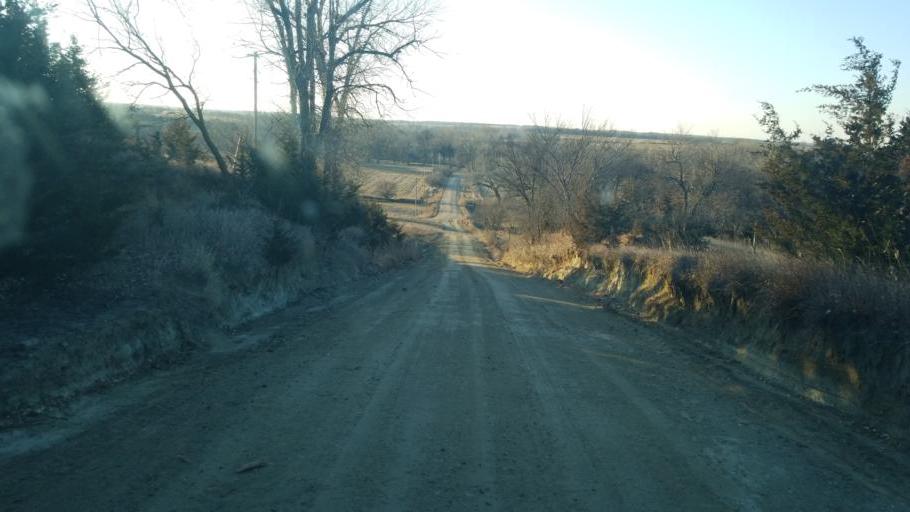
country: US
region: Nebraska
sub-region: Knox County
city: Center
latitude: 42.5592
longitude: -97.7986
